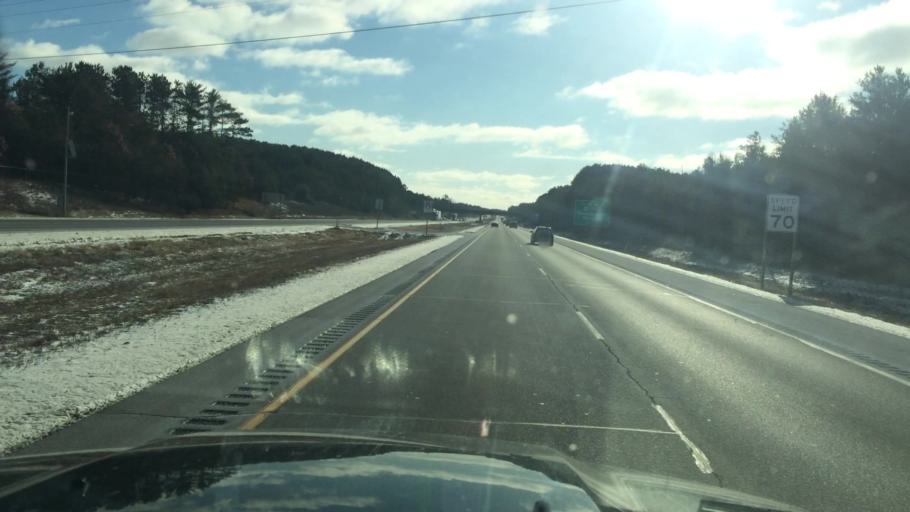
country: US
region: Wisconsin
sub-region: Portage County
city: Stevens Point
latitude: 44.5345
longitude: -89.5385
